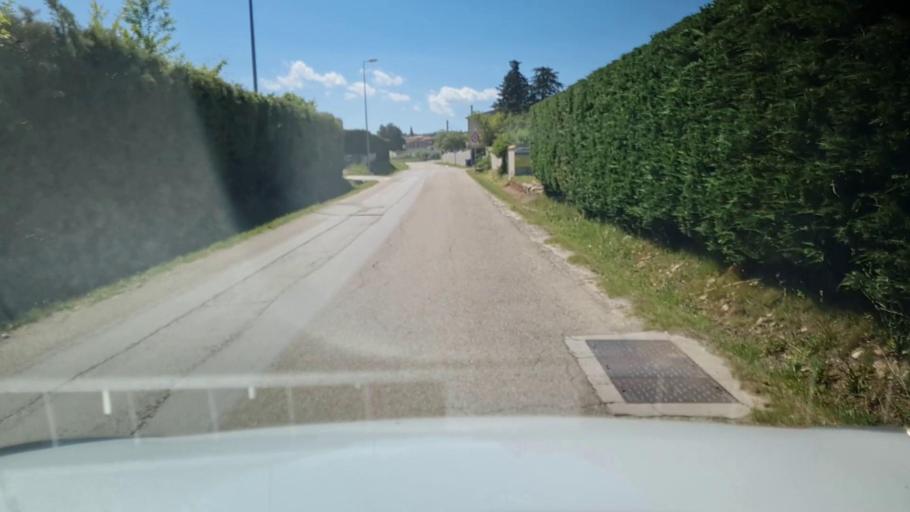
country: FR
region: Languedoc-Roussillon
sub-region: Departement du Gard
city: Saint-Mamert-du-Gard
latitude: 43.9091
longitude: 4.2002
